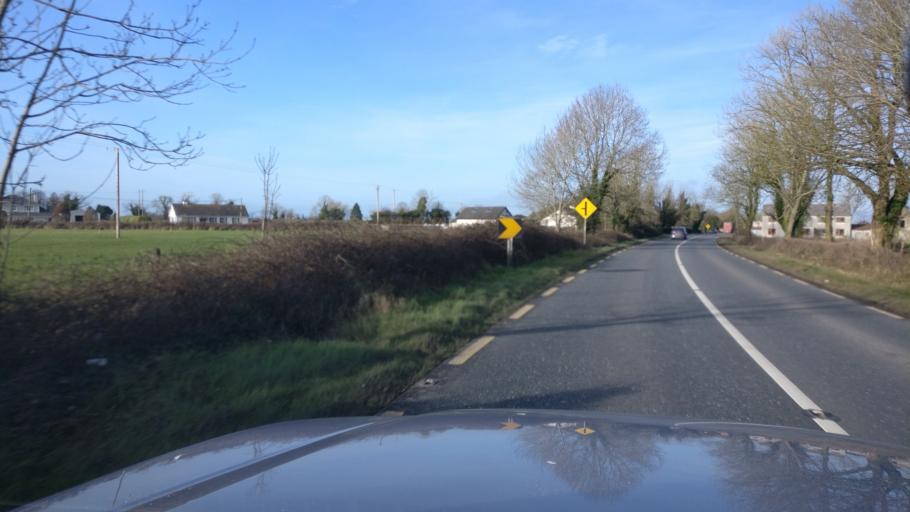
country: IE
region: Leinster
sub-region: Laois
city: Mountmellick
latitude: 53.1491
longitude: -7.3700
